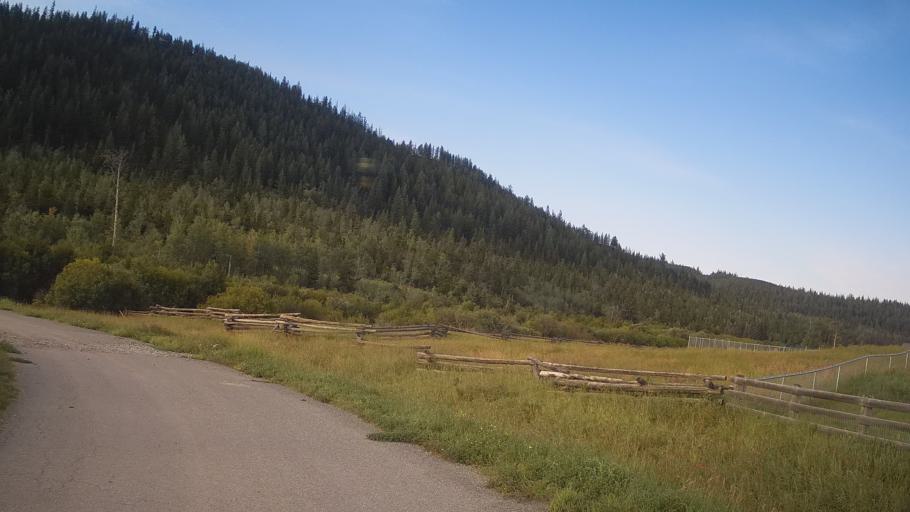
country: CA
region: British Columbia
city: Hanceville
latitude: 52.1361
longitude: -123.9504
